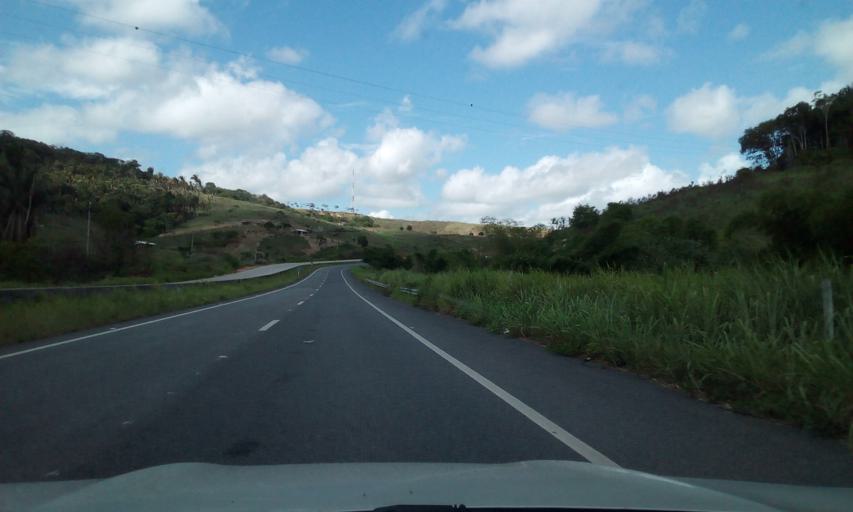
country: BR
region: Alagoas
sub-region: Rio Largo
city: Rio Largo
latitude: -9.4953
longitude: -35.9022
